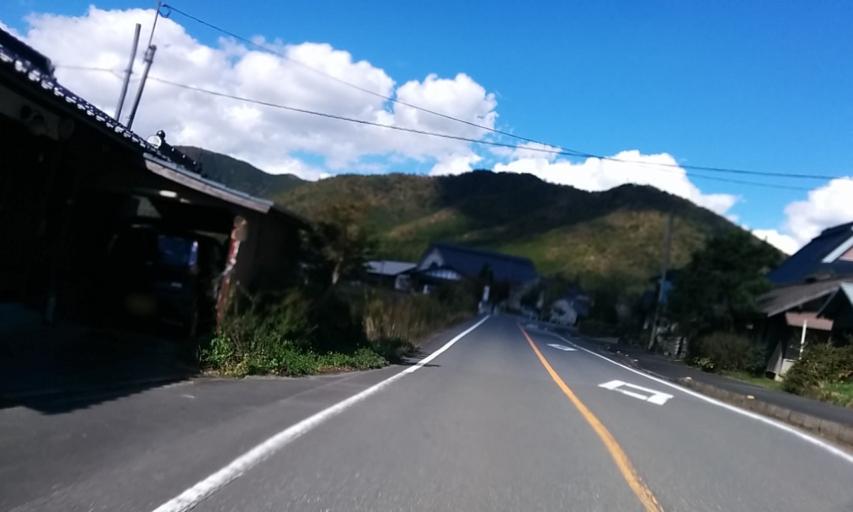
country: JP
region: Kyoto
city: Kameoka
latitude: 35.2693
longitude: 135.5498
